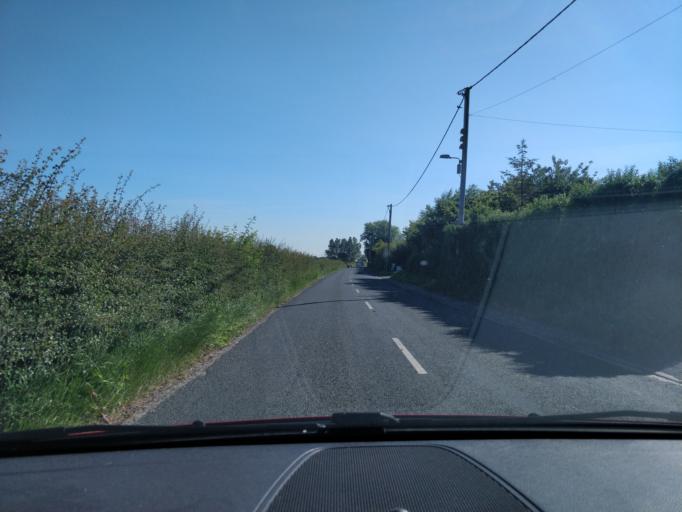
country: GB
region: England
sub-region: Lancashire
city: Banks
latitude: 53.6989
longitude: -2.8846
